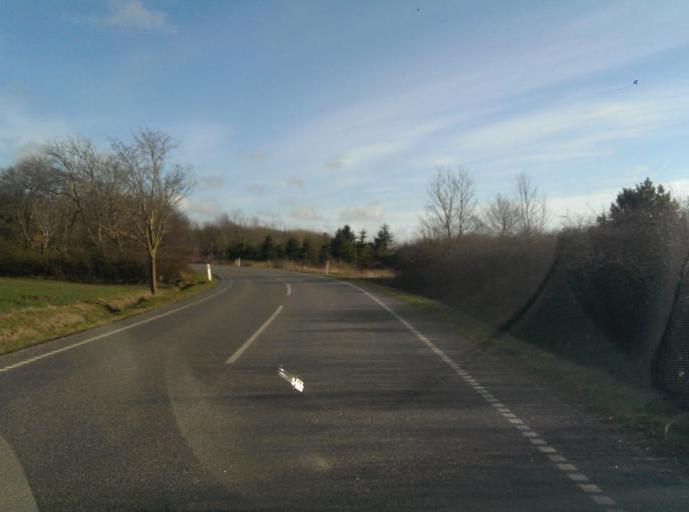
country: DK
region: South Denmark
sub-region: Esbjerg Kommune
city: Bramming
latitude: 55.4481
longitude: 8.6902
